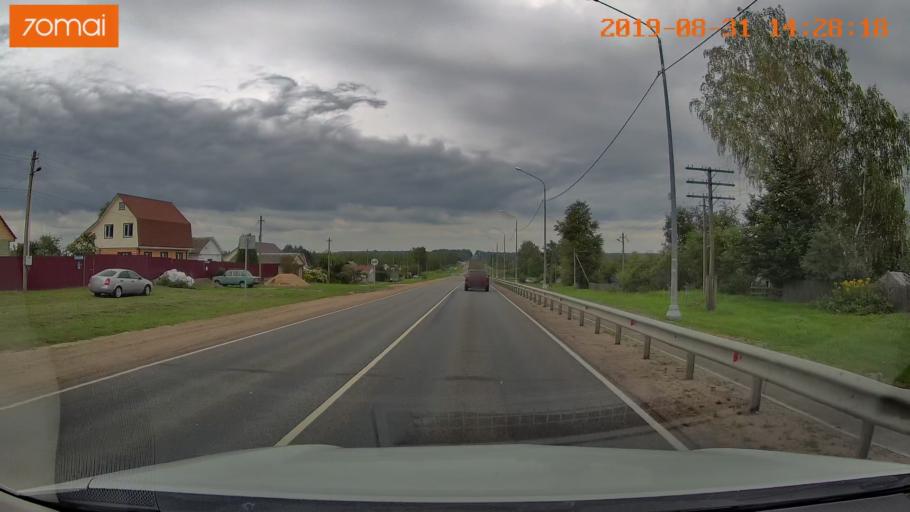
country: RU
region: Smolensk
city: Yekimovichi
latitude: 54.1197
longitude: 33.3112
